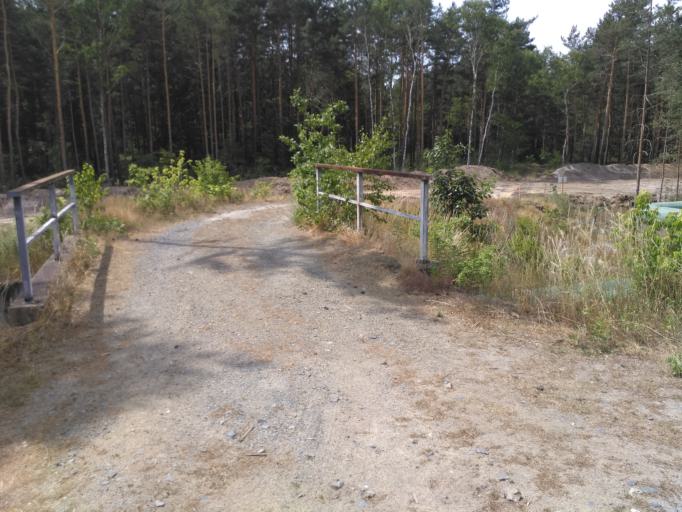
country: DE
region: Saxony
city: Hoyerswerda
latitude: 51.4490
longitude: 14.2981
